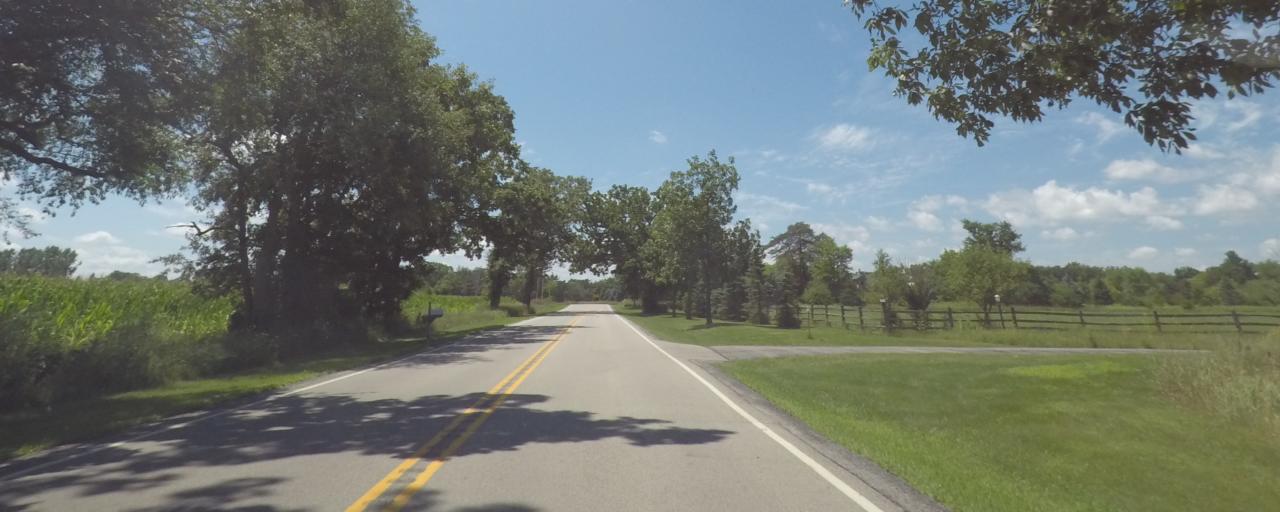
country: US
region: Wisconsin
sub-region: Waukesha County
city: Dousman
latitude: 42.9486
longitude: -88.4940
